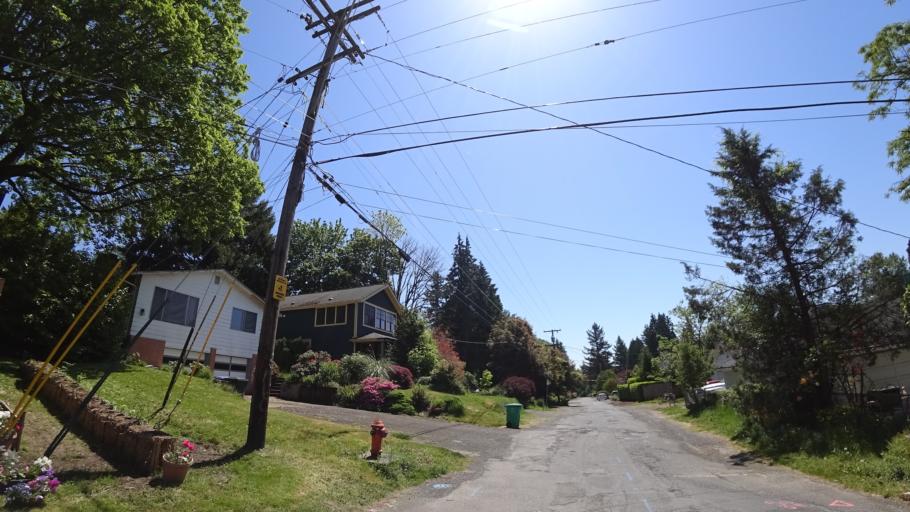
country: US
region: Oregon
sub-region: Multnomah County
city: Portland
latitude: 45.4742
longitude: -122.6835
